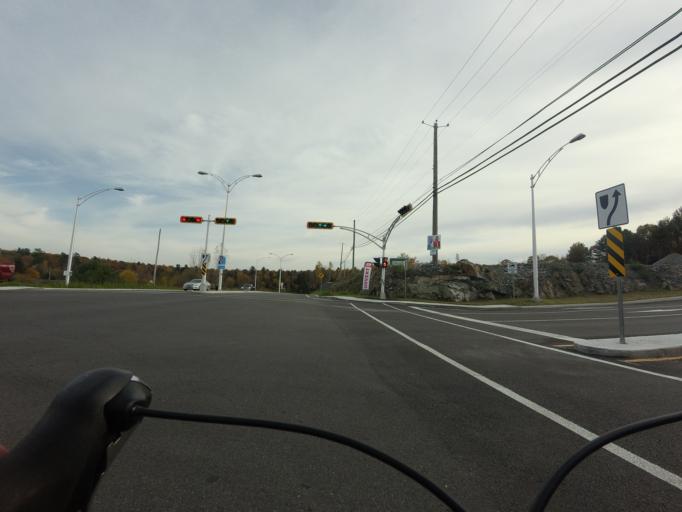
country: CA
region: Quebec
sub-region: Outaouais
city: Gatineau
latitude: 45.5393
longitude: -75.7721
